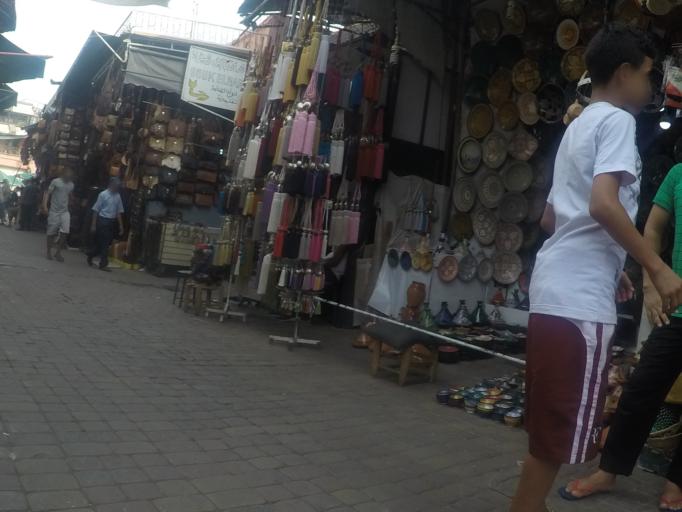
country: MA
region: Marrakech-Tensift-Al Haouz
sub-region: Marrakech
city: Marrakesh
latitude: 31.6269
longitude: -7.9879
